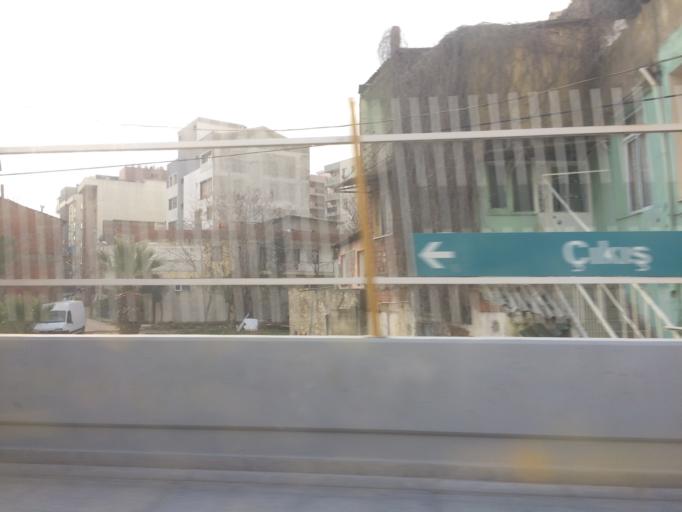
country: TR
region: Izmir
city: Karsiyaka
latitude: 38.4755
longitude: 27.0893
